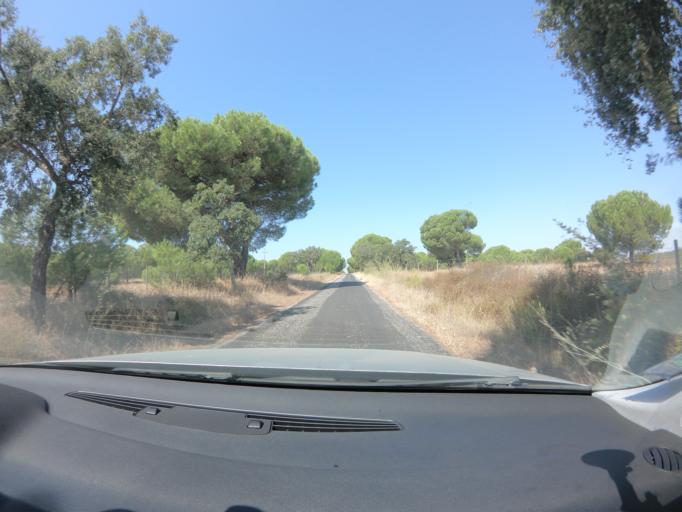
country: PT
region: Setubal
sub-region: Alcacer do Sal
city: Alcacer do Sal
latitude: 38.2564
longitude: -8.3029
